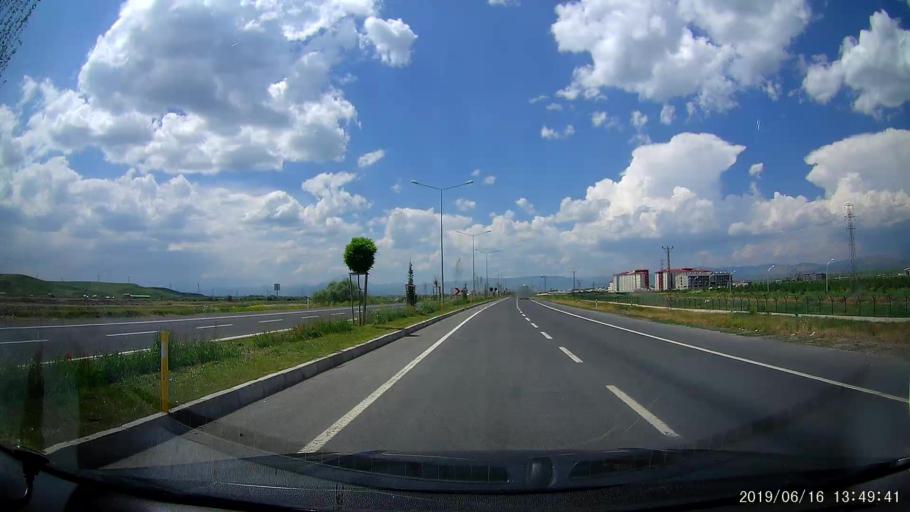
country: TR
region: Agri
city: Agri
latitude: 39.7192
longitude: 42.9877
